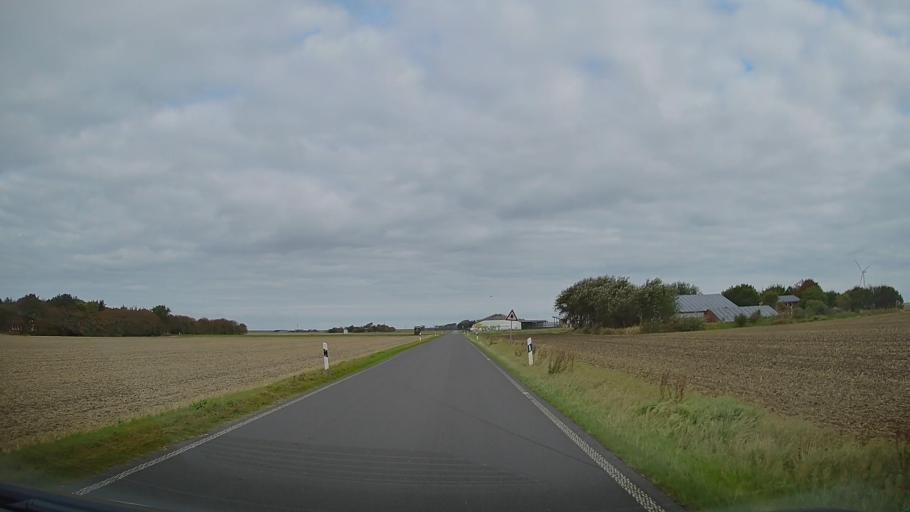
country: DE
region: Schleswig-Holstein
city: Friedrich-Wilhelm-Lubke-Koog
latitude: 54.8676
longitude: 8.6258
